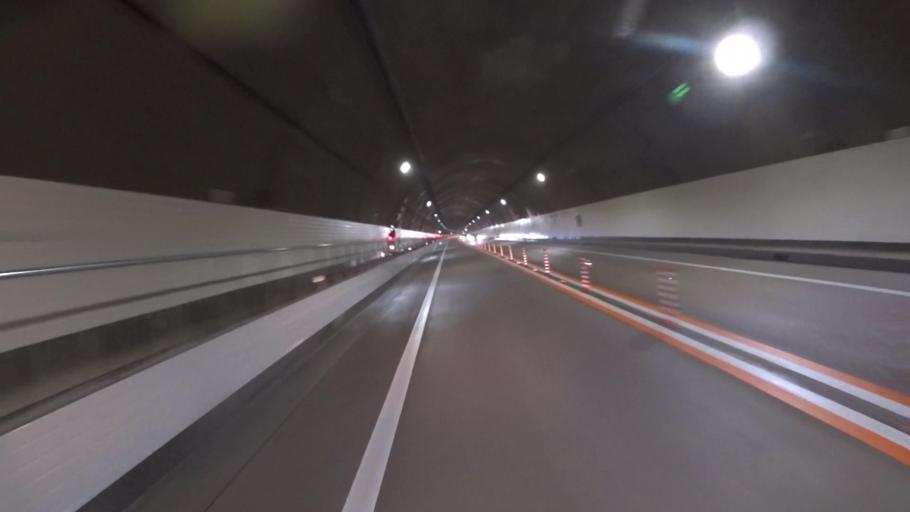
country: JP
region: Kyoto
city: Ayabe
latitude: 35.2438
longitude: 135.3428
